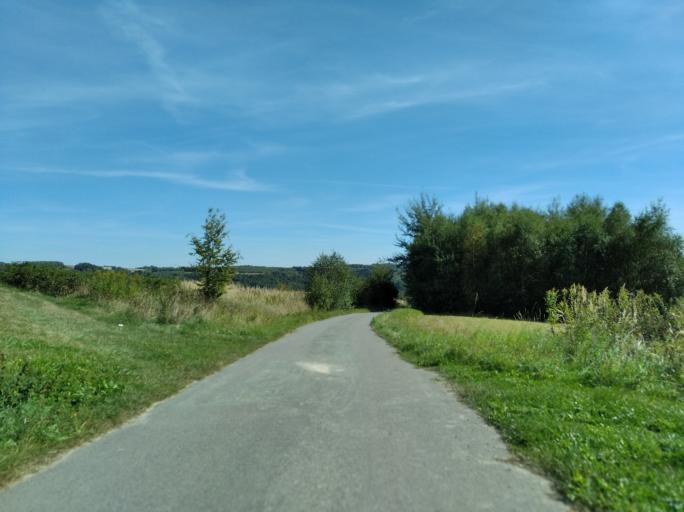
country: PL
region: Subcarpathian Voivodeship
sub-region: Powiat strzyzowski
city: Wisniowa
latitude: 49.8982
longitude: 21.6297
